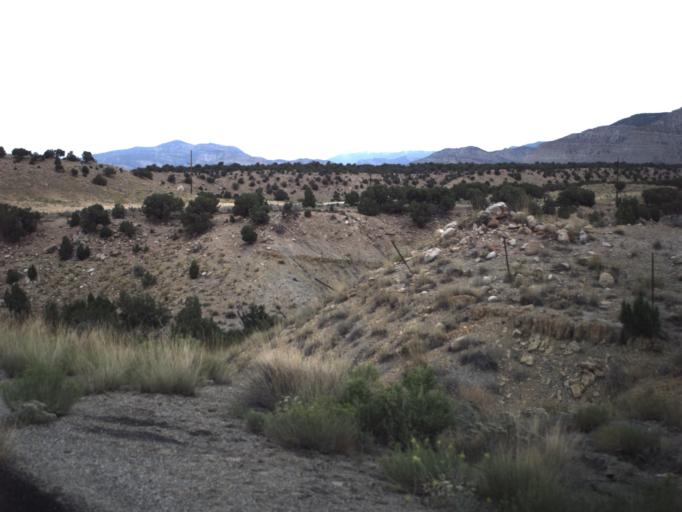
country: US
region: Utah
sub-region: Carbon County
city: East Carbon City
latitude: 39.4839
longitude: -110.4025
